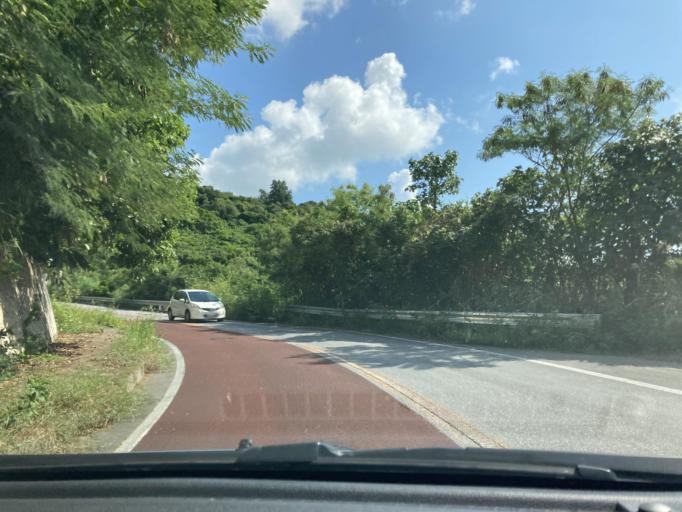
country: JP
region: Okinawa
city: Tomigusuku
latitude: 26.1391
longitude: 127.7746
